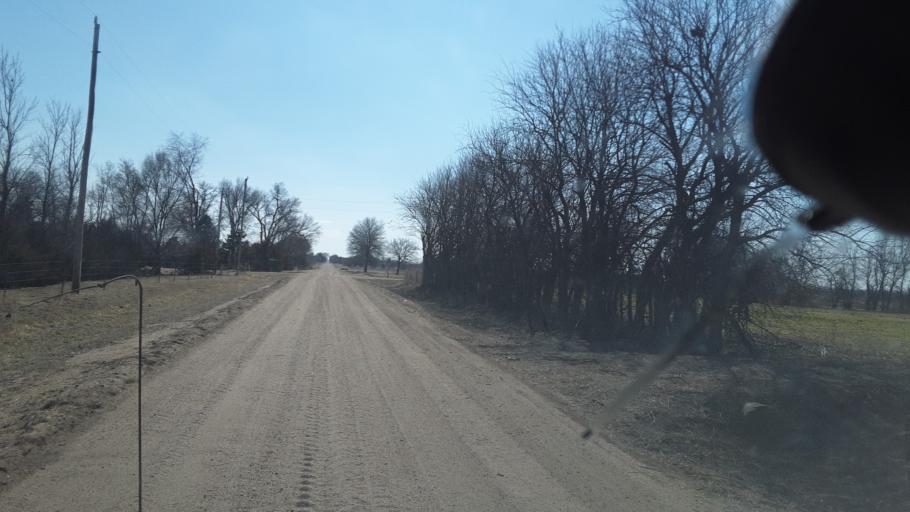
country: US
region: Kansas
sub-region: Reno County
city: Haven
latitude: 37.9275
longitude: -97.8485
